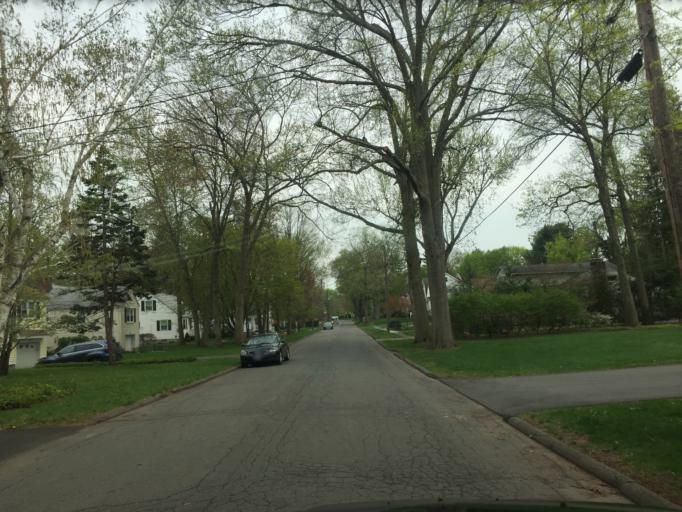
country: US
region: Connecticut
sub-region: Hartford County
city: Newington
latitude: 41.6845
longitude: -72.7399
